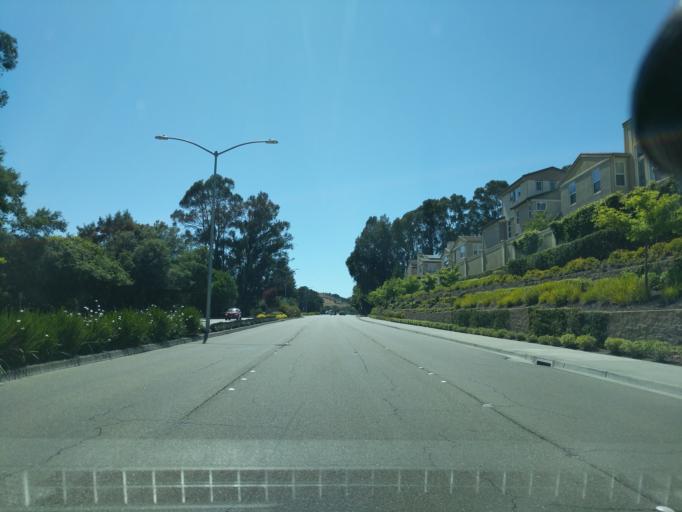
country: US
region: California
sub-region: Contra Costa County
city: San Ramon
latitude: 37.7739
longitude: -121.9857
